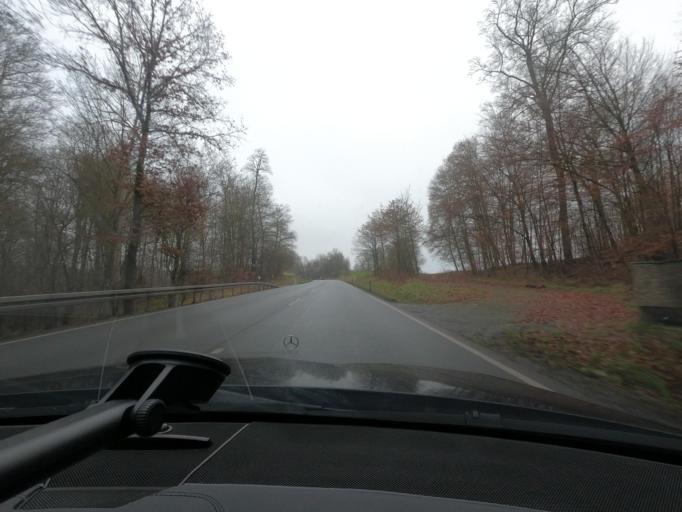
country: DE
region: Hesse
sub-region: Regierungsbezirk Kassel
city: Bad Arolsen
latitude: 51.3545
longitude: 9.0681
